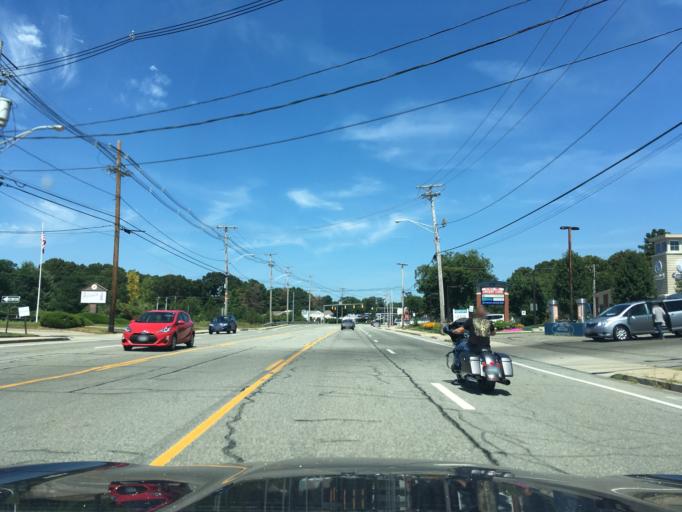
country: US
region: Rhode Island
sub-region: Kent County
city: East Greenwich
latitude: 41.6382
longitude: -71.4686
